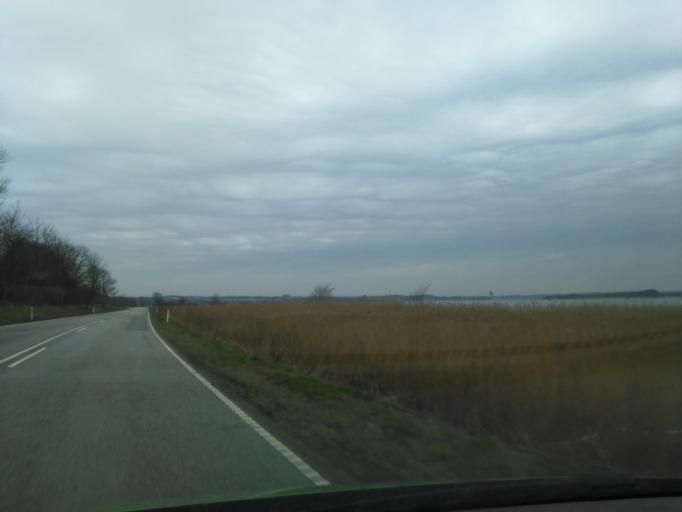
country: DK
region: North Denmark
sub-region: Mariagerfjord Kommune
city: Hadsund
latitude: 56.6943
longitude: 10.1101
